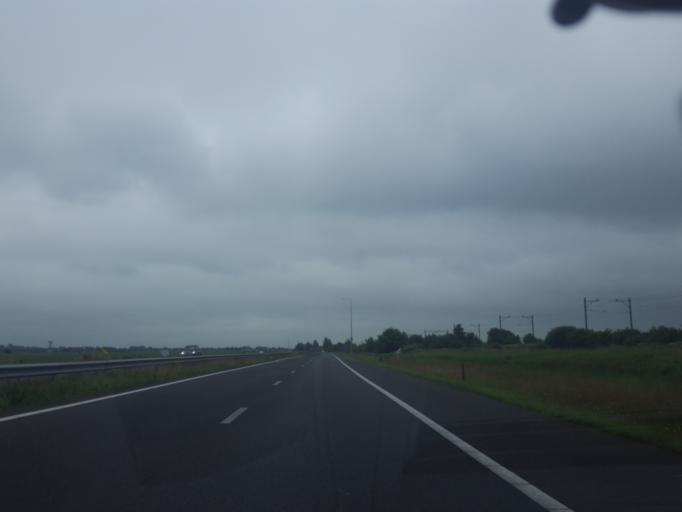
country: NL
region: Friesland
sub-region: Gemeente Boarnsterhim
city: Grou
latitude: 53.0750
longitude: 5.8309
